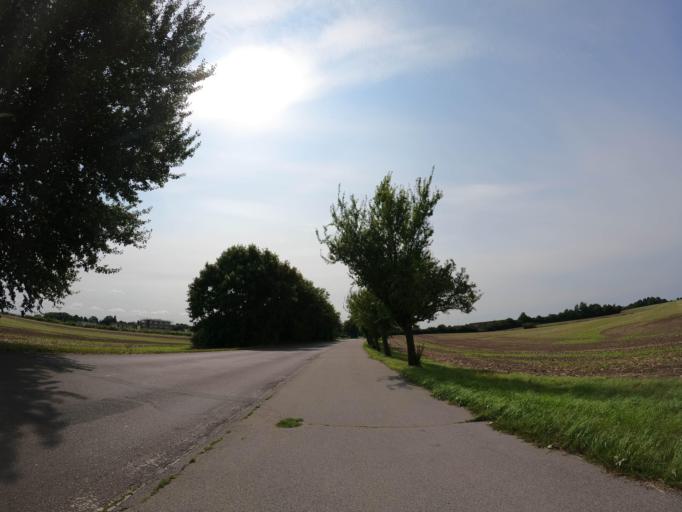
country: DE
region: Mecklenburg-Vorpommern
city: Kramerhof
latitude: 54.3453
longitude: 13.0689
